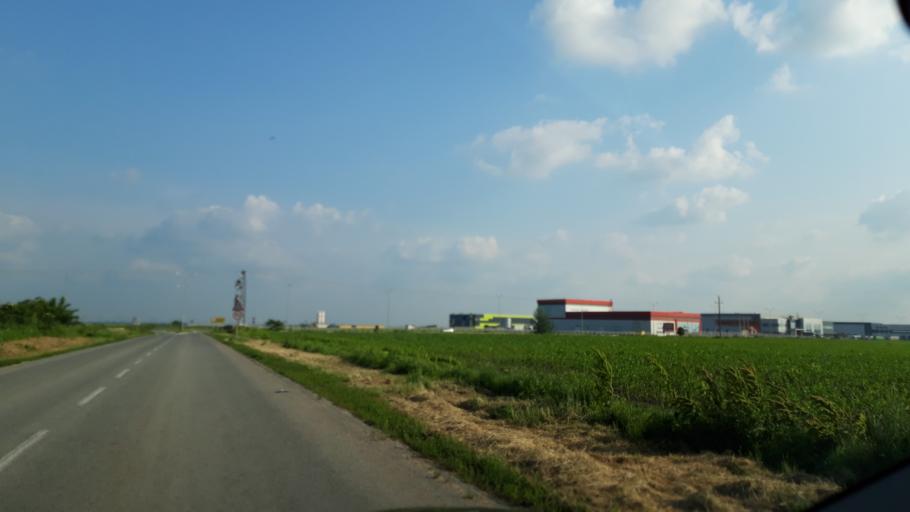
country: RS
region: Autonomna Pokrajina Vojvodina
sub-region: Sremski Okrug
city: Ingija
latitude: 45.0659
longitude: 20.1276
